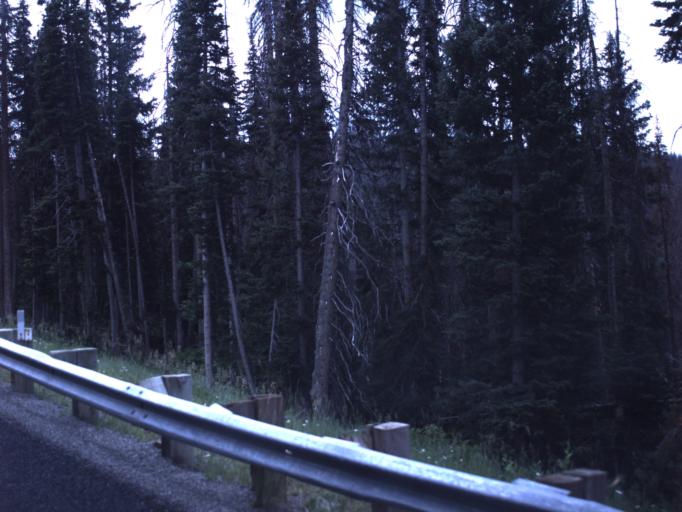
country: US
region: Utah
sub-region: Summit County
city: Francis
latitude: 40.4864
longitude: -111.0339
